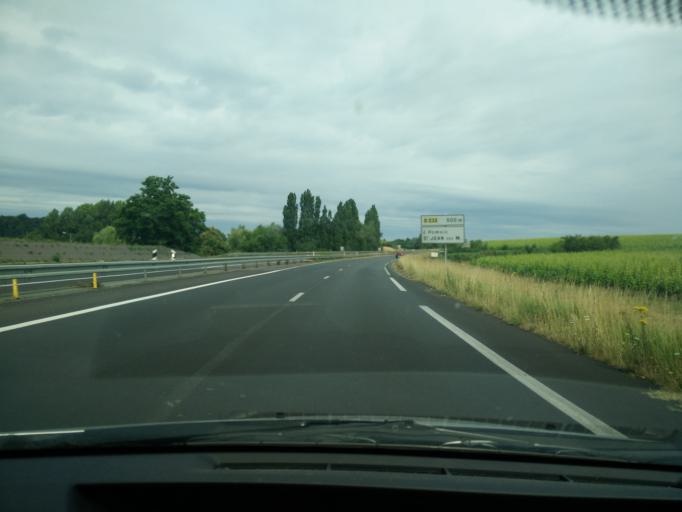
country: FR
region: Pays de la Loire
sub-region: Departement de Maine-et-Loire
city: Brissac-Quince
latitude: 47.3677
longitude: -0.4573
